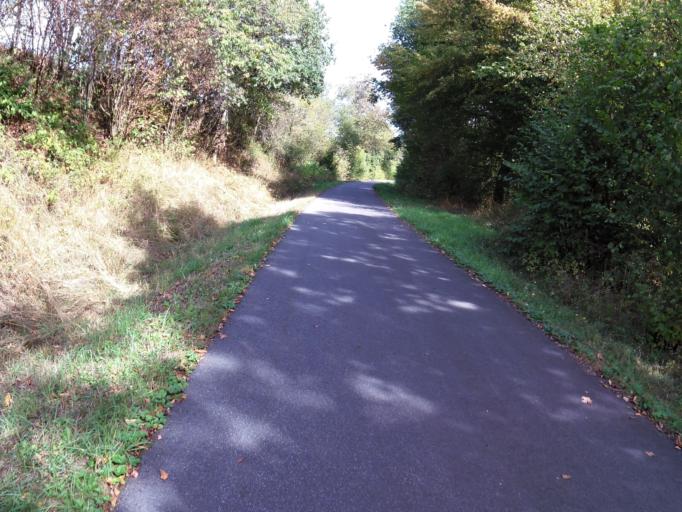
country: DE
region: Rheinland-Pfalz
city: Kickeshausen
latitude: 50.0650
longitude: 6.2478
